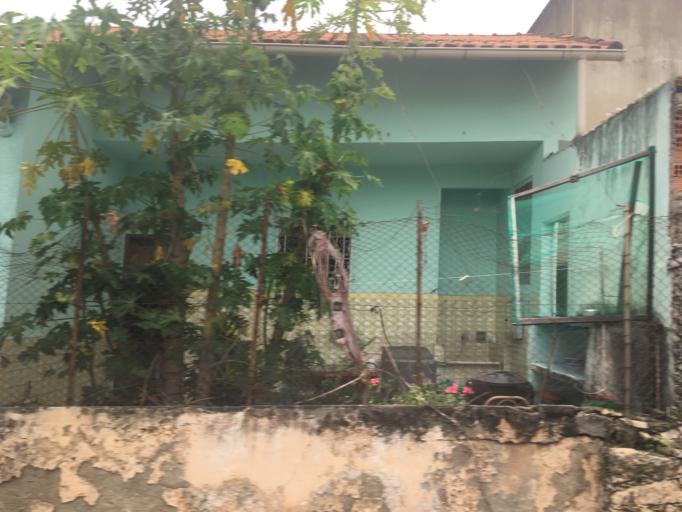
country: BR
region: Rio de Janeiro
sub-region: Rio De Janeiro
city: Rio de Janeiro
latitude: -22.9017
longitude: -43.2567
